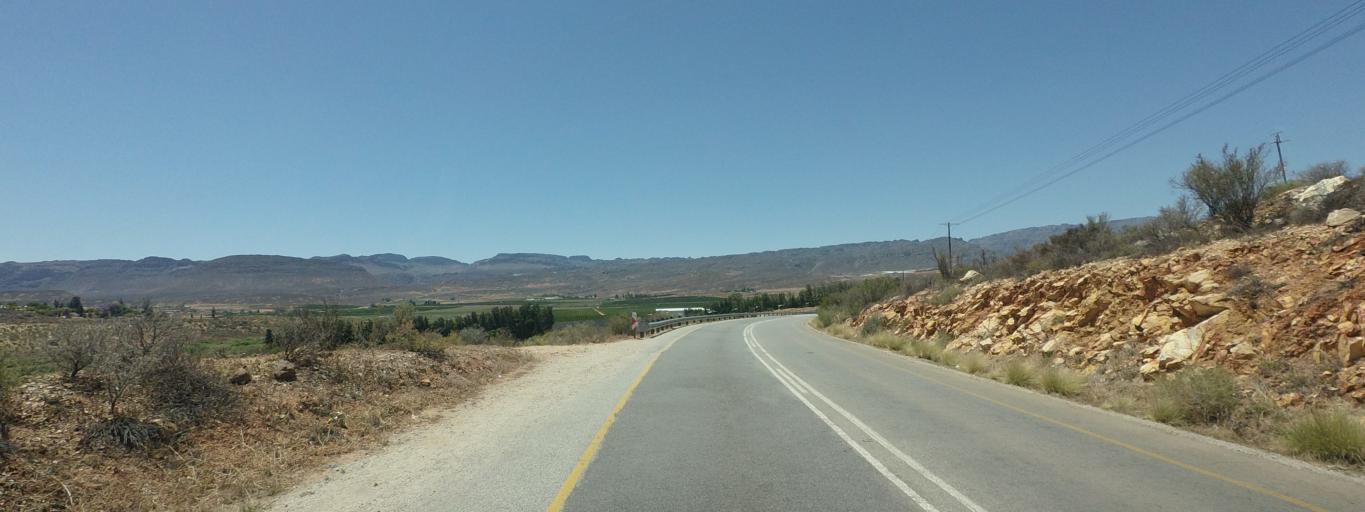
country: ZA
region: Western Cape
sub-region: West Coast District Municipality
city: Clanwilliam
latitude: -32.1705
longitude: 18.8741
